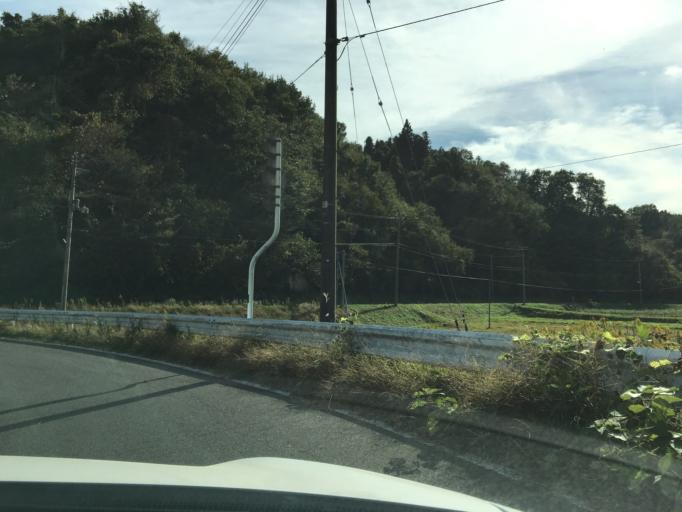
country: JP
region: Fukushima
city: Nihommatsu
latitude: 37.5234
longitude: 140.5022
